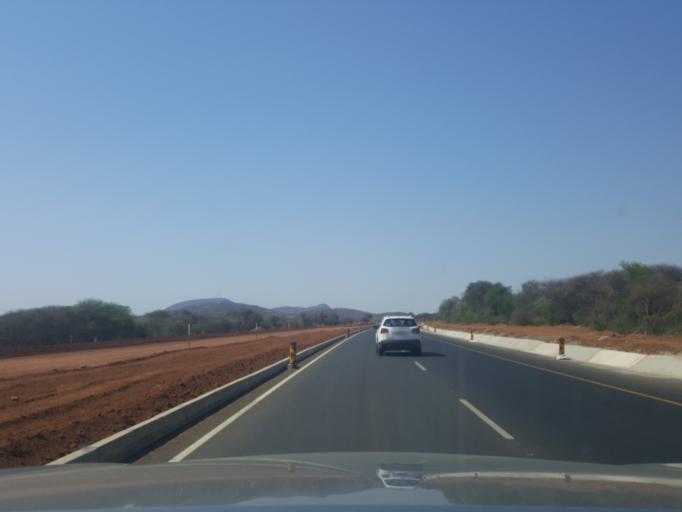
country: BW
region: South East
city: Ramotswa
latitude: -24.7750
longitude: 25.8267
